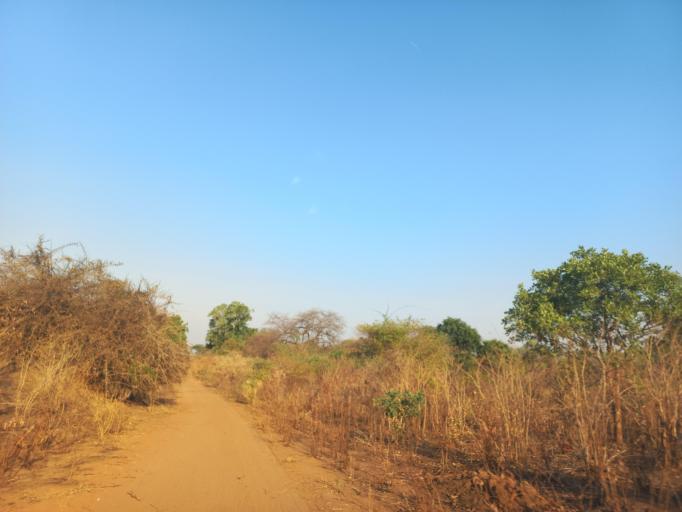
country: ZM
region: Lusaka
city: Luangwa
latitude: -15.4214
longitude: 30.2787
